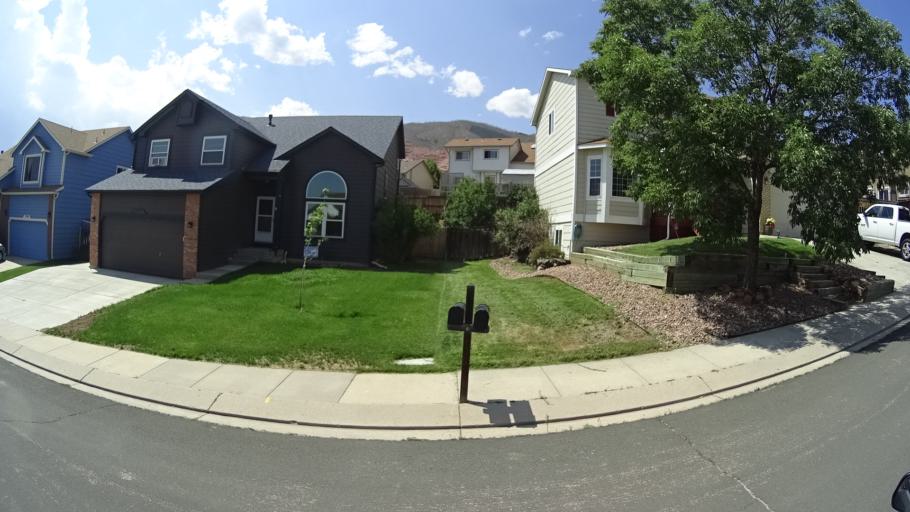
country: US
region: Colorado
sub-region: El Paso County
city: Air Force Academy
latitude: 38.9377
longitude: -104.8794
